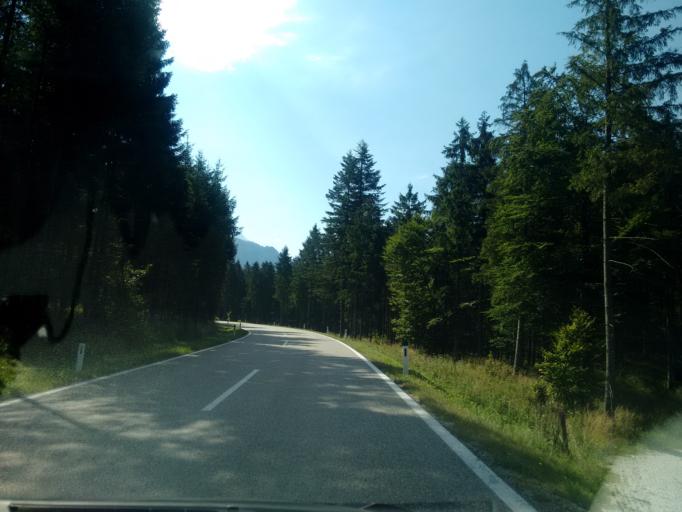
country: AT
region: Upper Austria
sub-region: Politischer Bezirk Gmunden
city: Gruenau im Almtal
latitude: 47.7988
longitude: 13.9535
